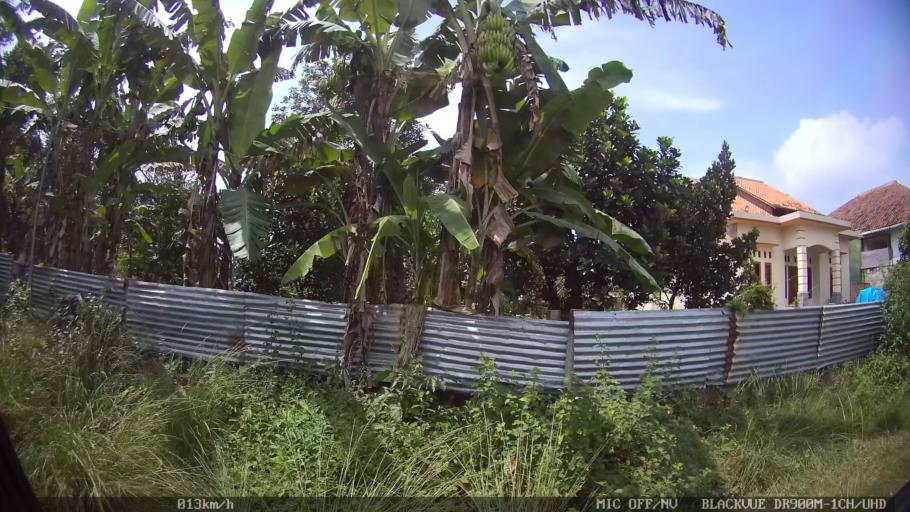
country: ID
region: Lampung
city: Kedaton
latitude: -5.3316
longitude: 105.2946
